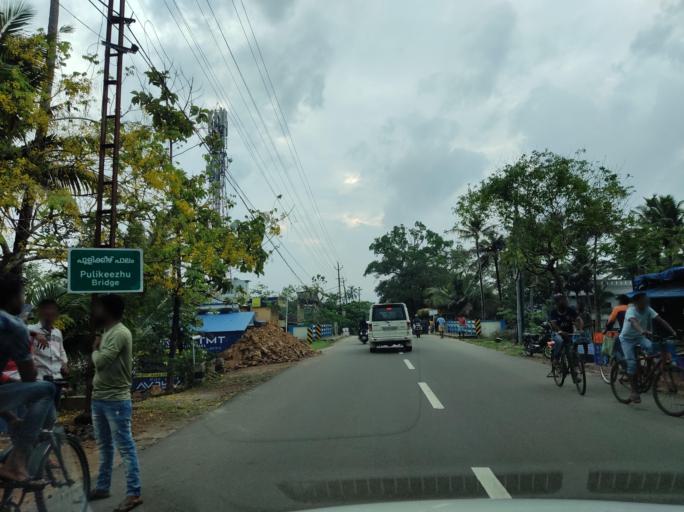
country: IN
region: Kerala
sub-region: Alappuzha
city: Kayankulam
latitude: 9.2579
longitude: 76.4245
